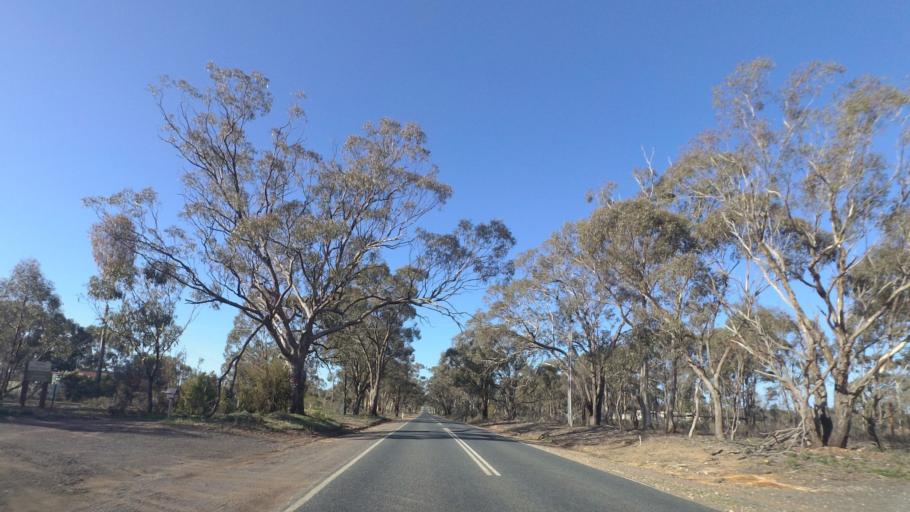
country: AU
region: Victoria
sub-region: Greater Bendigo
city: Epsom
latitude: -36.6767
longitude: 144.3891
